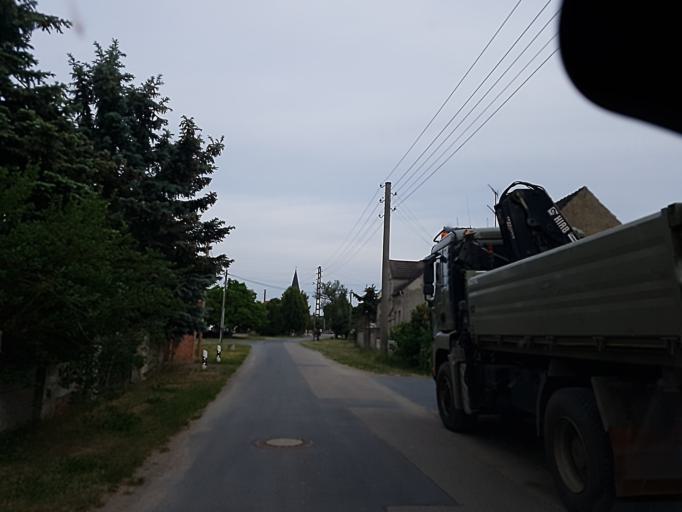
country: DE
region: Brandenburg
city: Herzberg
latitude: 51.6600
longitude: 13.2771
